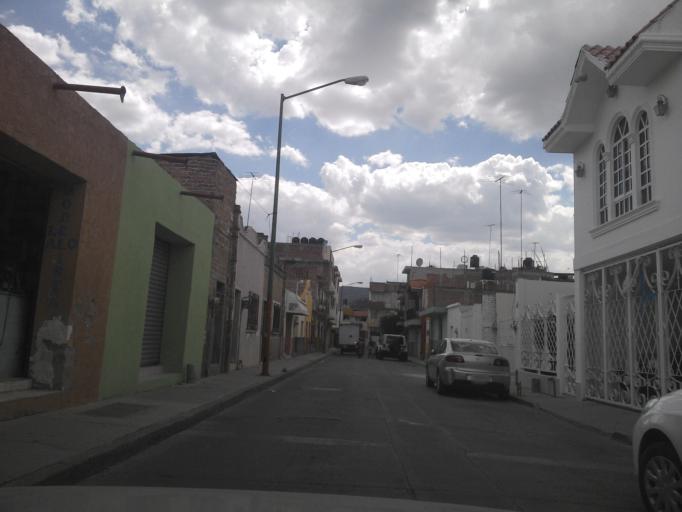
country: MX
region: Guanajuato
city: San Francisco del Rincon
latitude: 21.0240
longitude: -101.8585
